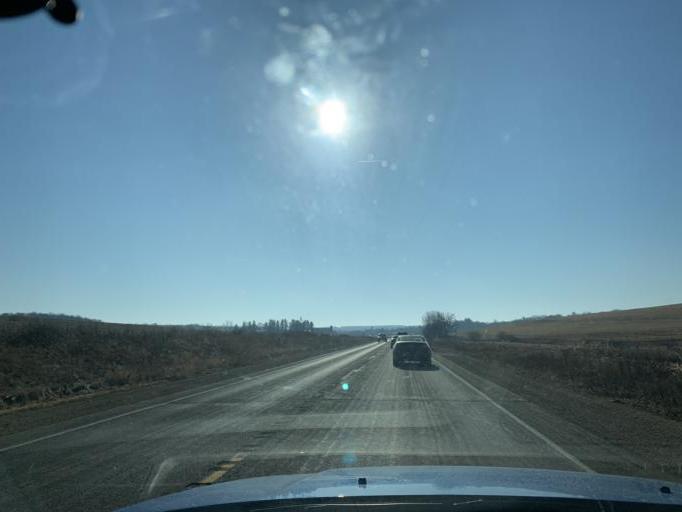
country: US
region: Wisconsin
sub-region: Green County
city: New Glarus
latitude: 42.8329
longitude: -89.6350
